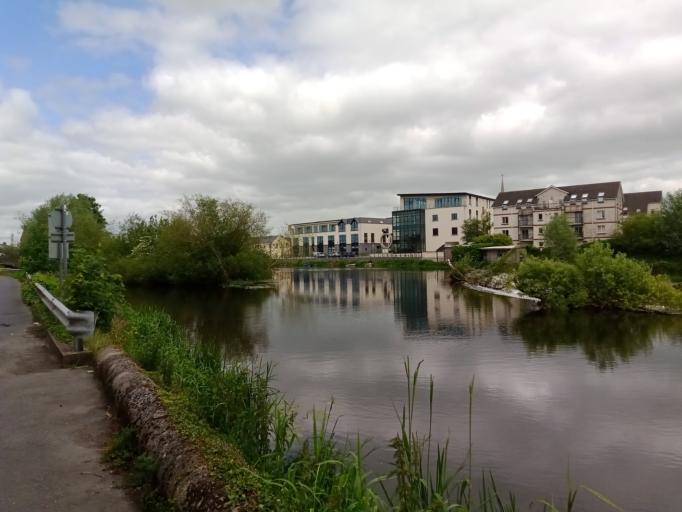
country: IE
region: Leinster
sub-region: County Carlow
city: Carlow
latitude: 52.8352
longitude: -6.9385
